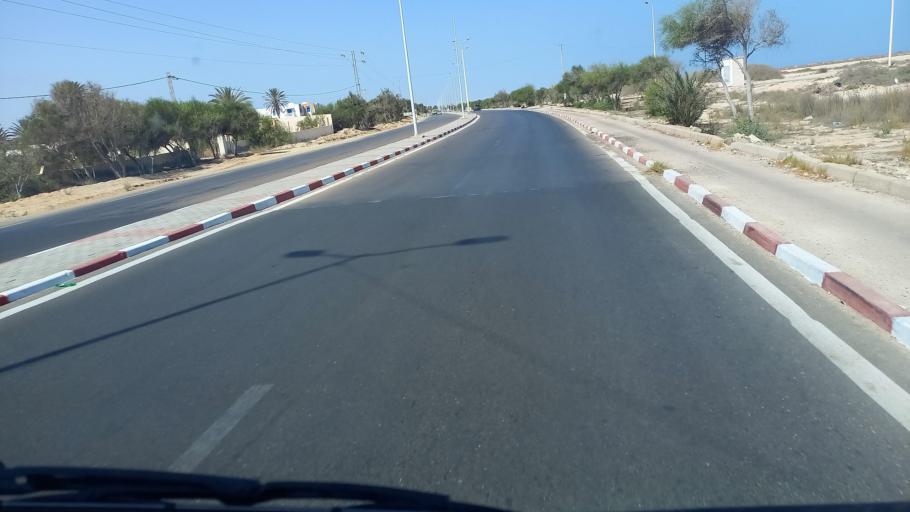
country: TN
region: Madanin
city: Midoun
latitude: 33.8692
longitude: 10.9545
